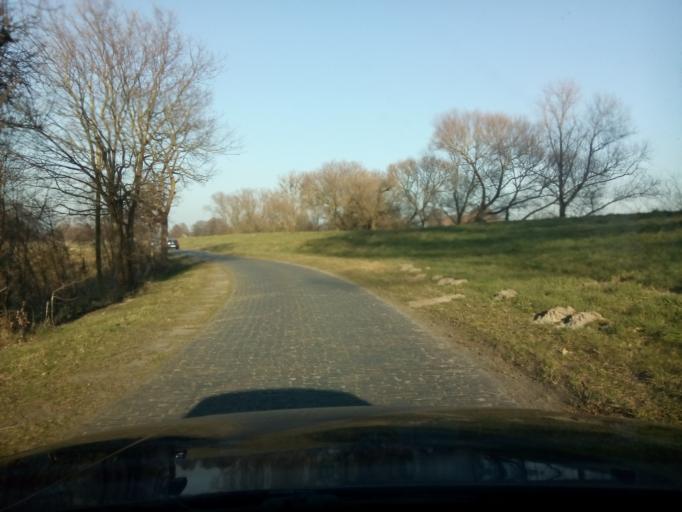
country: DE
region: Lower Saxony
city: Lilienthal
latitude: 53.1340
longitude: 8.8819
